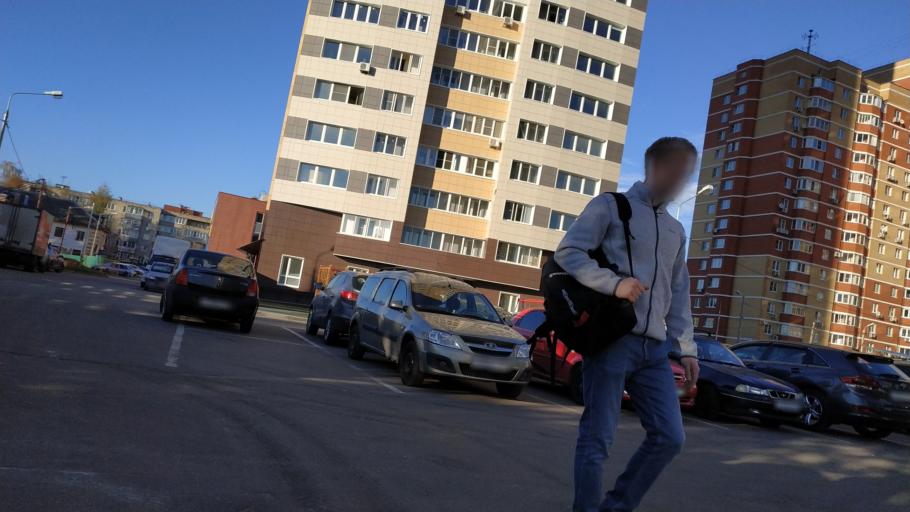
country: RU
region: Moskovskaya
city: Lobnya
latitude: 56.0055
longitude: 37.4644
